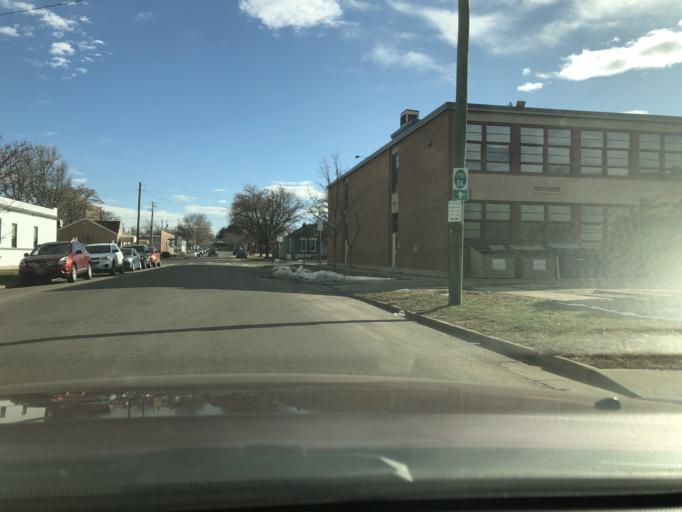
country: US
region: Colorado
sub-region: Denver County
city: Denver
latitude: 39.7587
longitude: -104.9759
